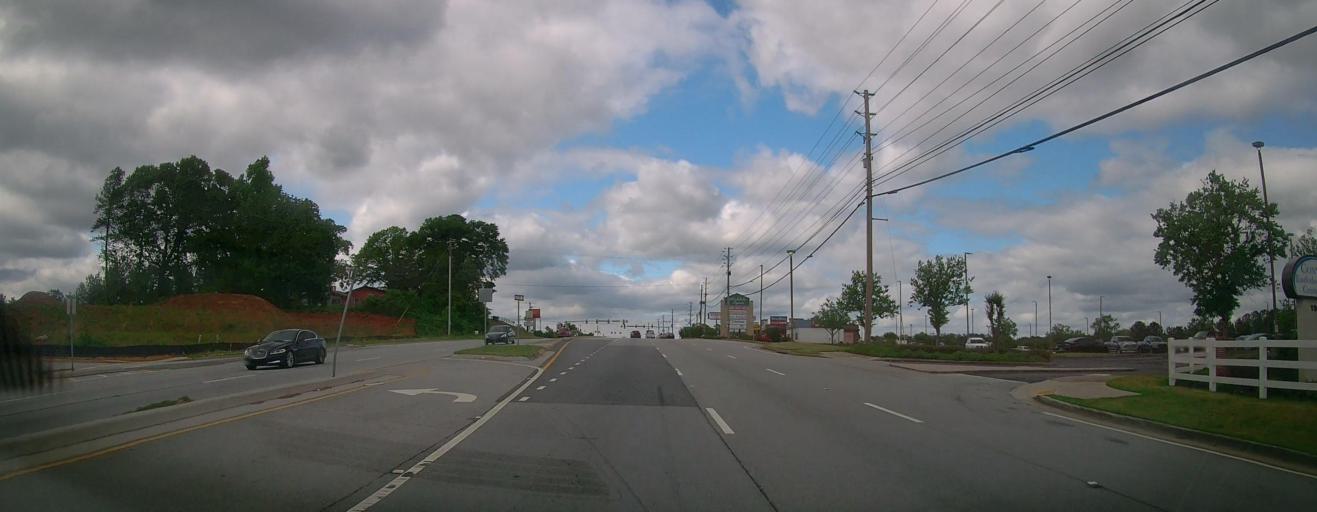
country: US
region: Georgia
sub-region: Rockdale County
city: Conyers
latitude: 33.6356
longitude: -84.0143
